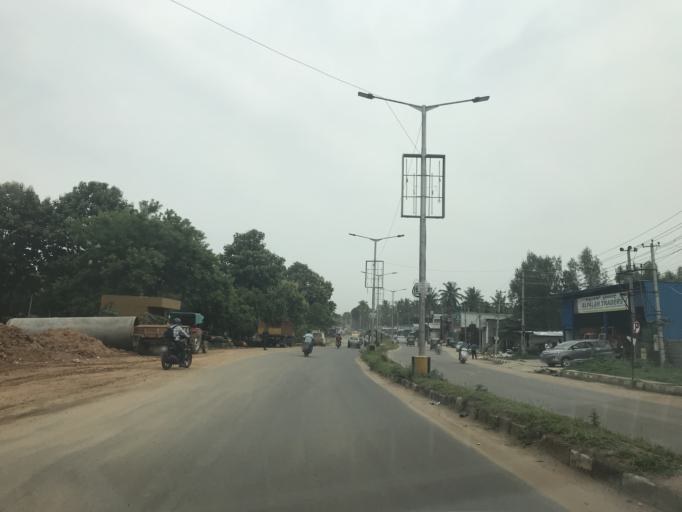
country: IN
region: Karnataka
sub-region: Bangalore Urban
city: Yelahanka
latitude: 13.0547
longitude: 77.6466
